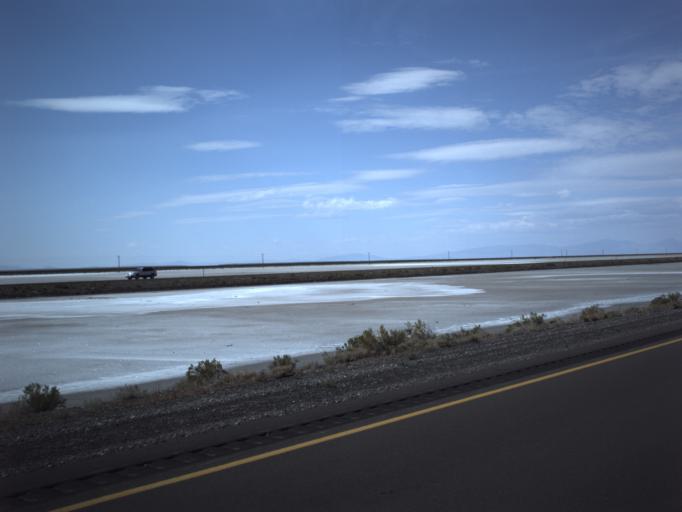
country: US
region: Utah
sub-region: Tooele County
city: Wendover
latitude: 40.7304
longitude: -113.4406
